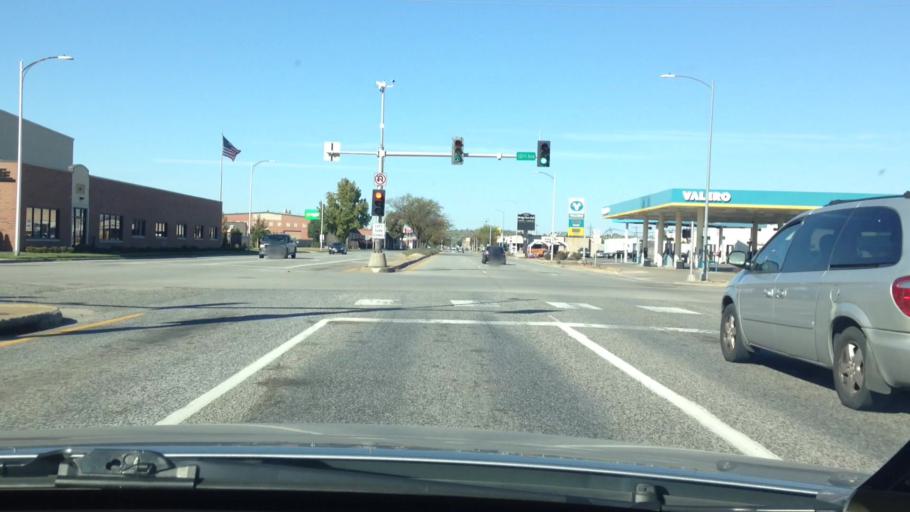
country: US
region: Missouri
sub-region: Clay County
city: North Kansas City
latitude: 39.1267
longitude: -94.5806
